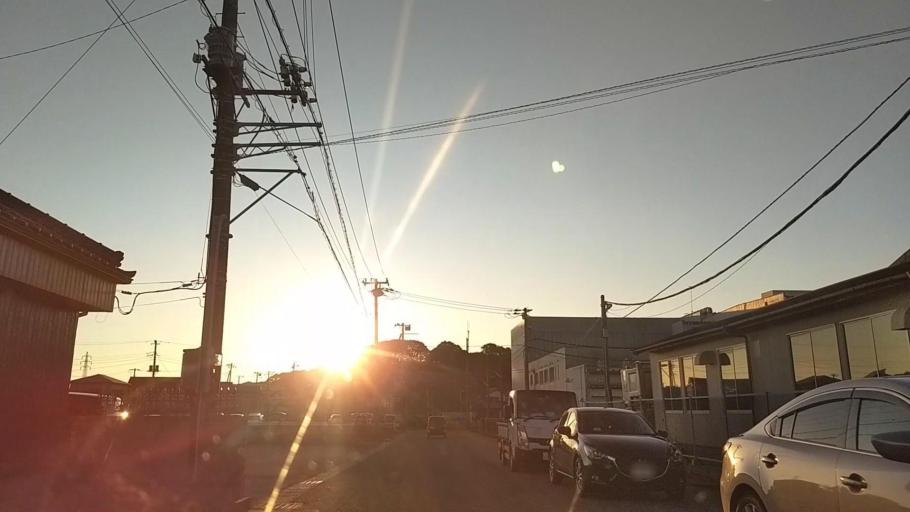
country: JP
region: Chiba
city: Hasaki
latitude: 35.7210
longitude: 140.8348
